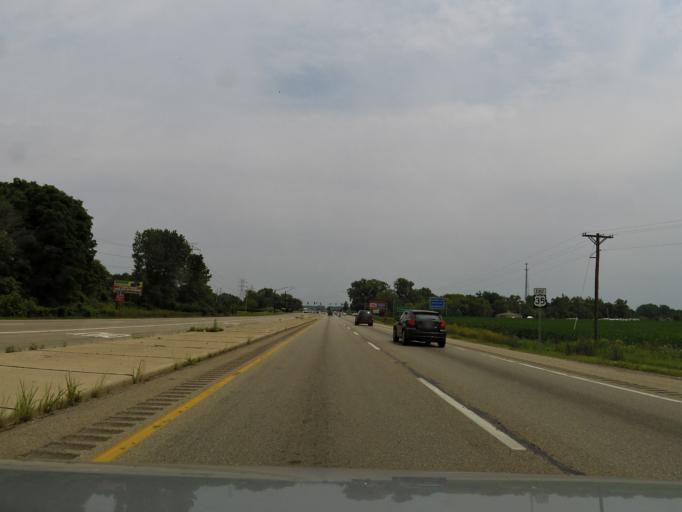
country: US
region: Ohio
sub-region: Greene County
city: Beavercreek
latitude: 39.7101
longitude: -84.0324
